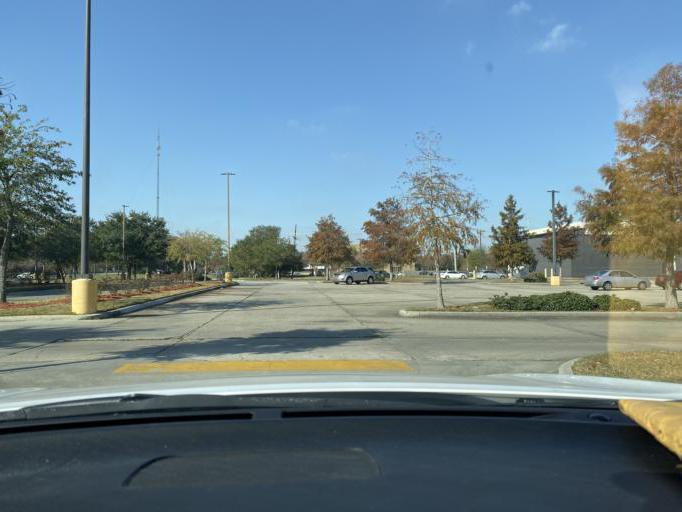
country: US
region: Louisiana
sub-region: Jefferson Parish
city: Terrytown
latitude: 29.9222
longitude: -90.0128
